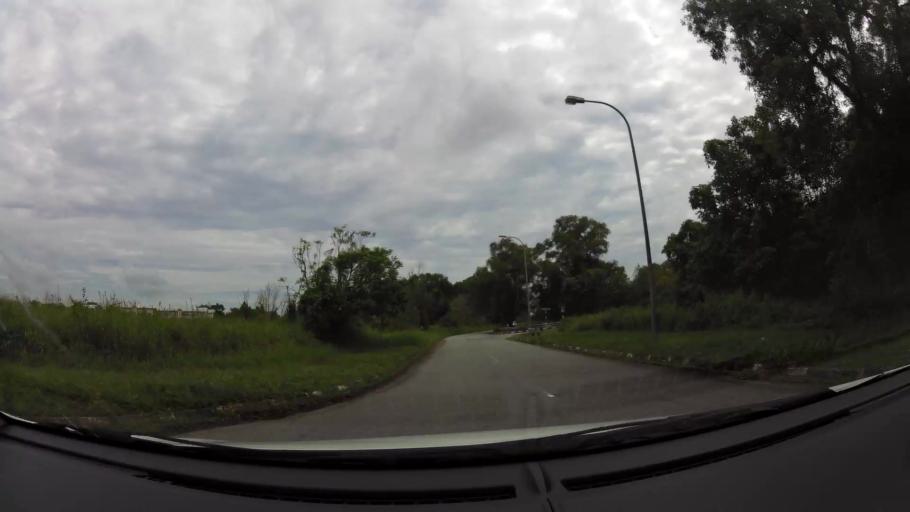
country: BN
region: Brunei and Muara
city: Bandar Seri Begawan
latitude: 4.9007
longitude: 114.9061
